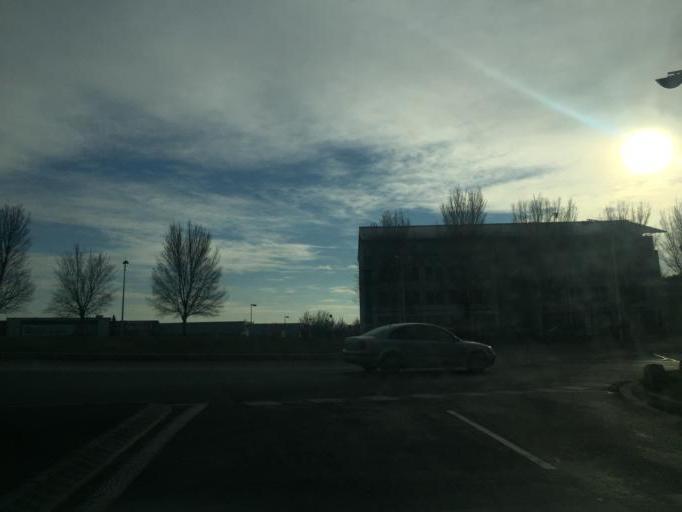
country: FR
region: Rhone-Alpes
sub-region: Departement du Rhone
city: Villefranche-sur-Saone
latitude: 45.9792
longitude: 4.7187
